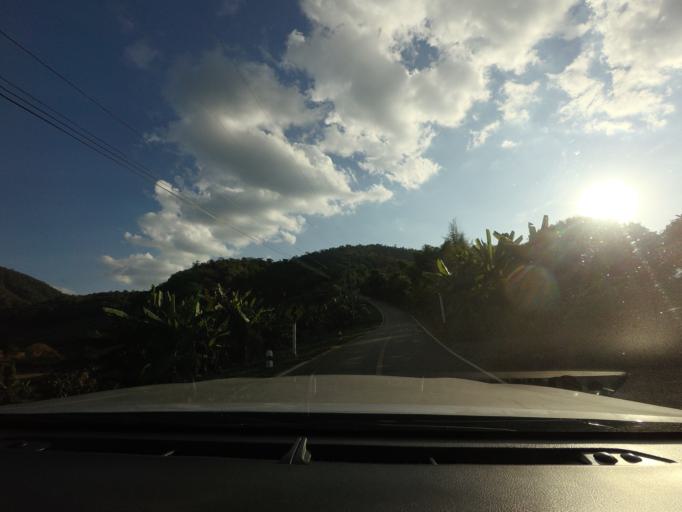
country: TH
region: Chiang Mai
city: Phrao
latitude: 19.5117
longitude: 99.1732
